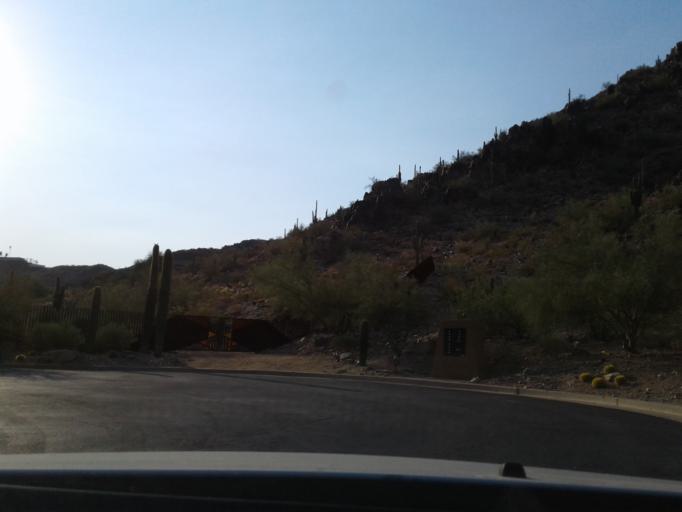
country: US
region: Arizona
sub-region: Maricopa County
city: Paradise Valley
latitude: 33.5414
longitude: -111.9949
